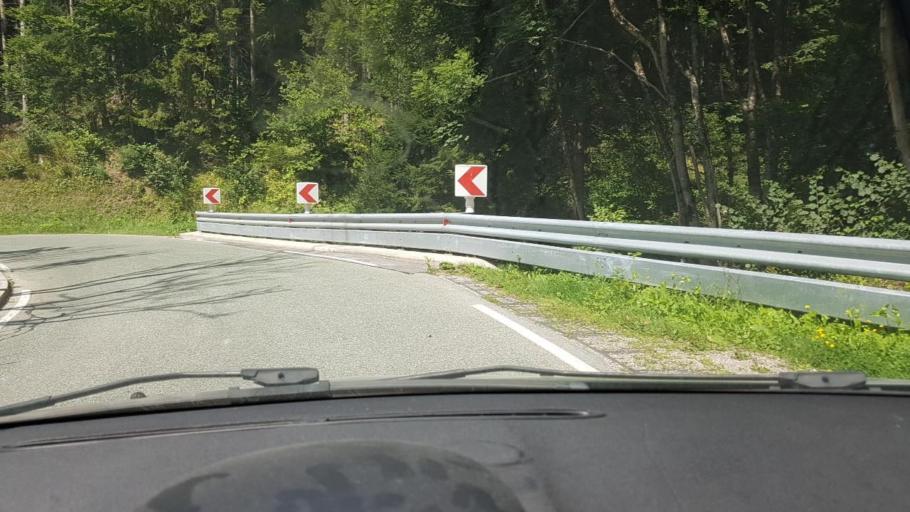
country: SI
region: Jezersko
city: Zgornje Jezersko
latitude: 46.4093
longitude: 14.5241
